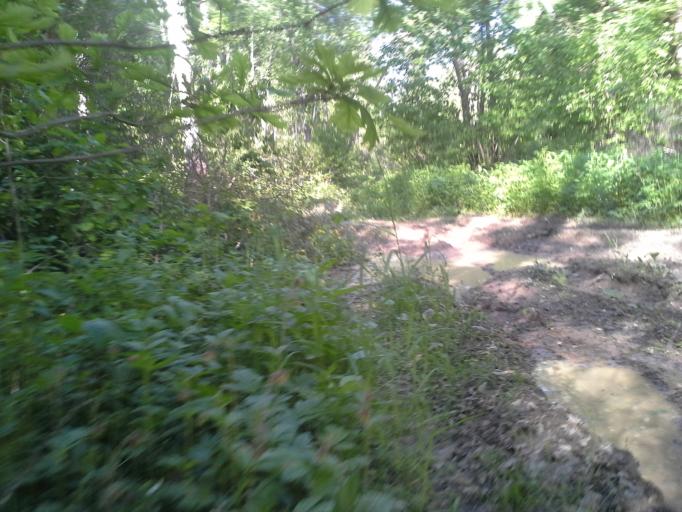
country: RU
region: Moskovskaya
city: Vatutinki
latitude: 55.4650
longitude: 37.4042
